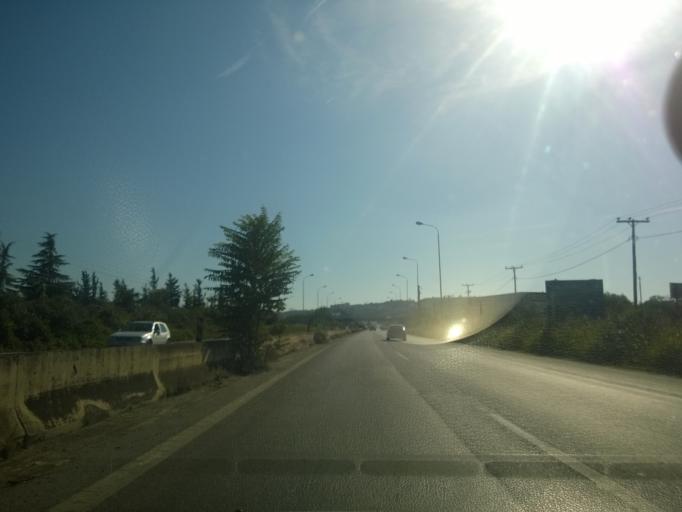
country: GR
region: Central Macedonia
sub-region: Nomos Thessalonikis
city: Neo Rysi
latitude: 40.4992
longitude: 23.0038
